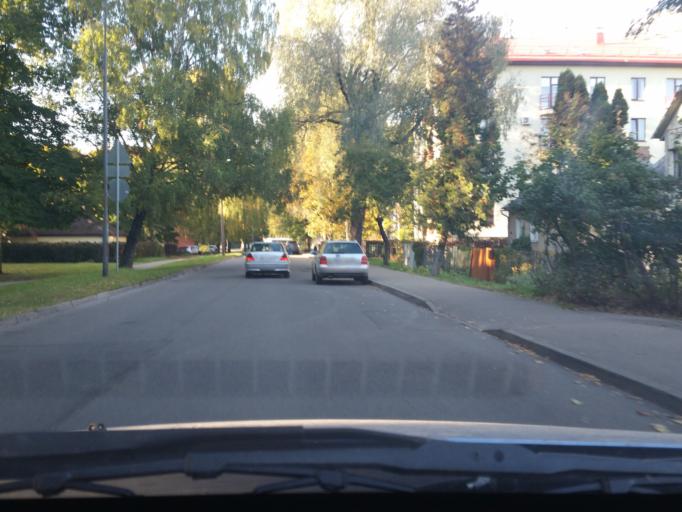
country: LV
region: Riga
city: Jaunciems
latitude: 56.9637
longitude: 24.1795
